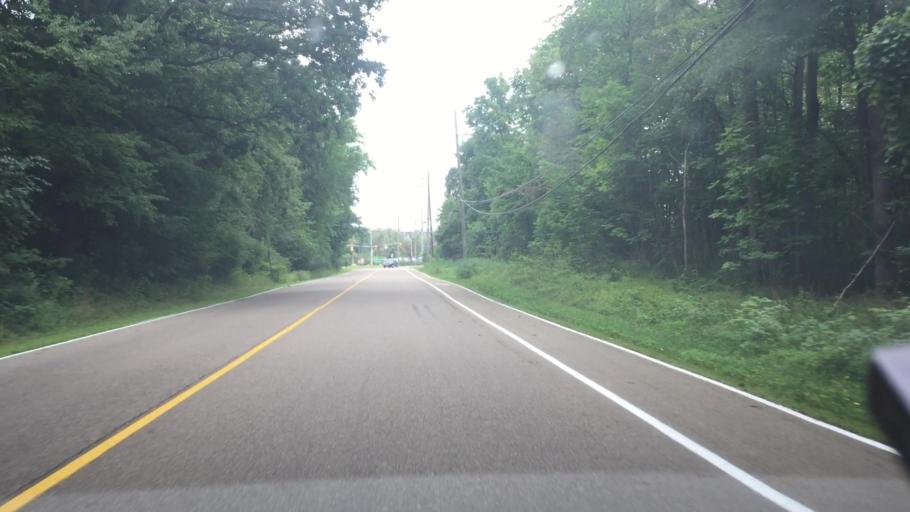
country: US
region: Michigan
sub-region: Oakland County
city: Auburn Hills
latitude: 42.6472
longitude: -83.2288
